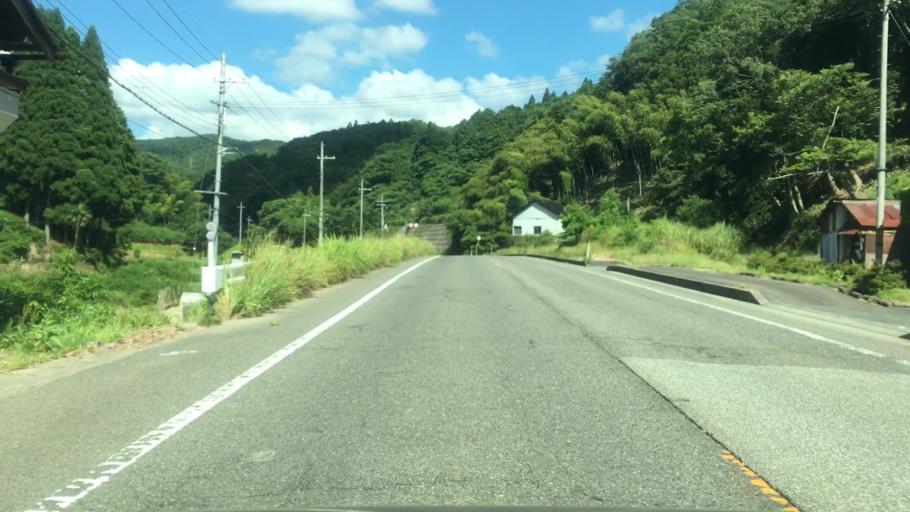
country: JP
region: Hyogo
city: Toyooka
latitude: 35.5751
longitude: 134.7643
